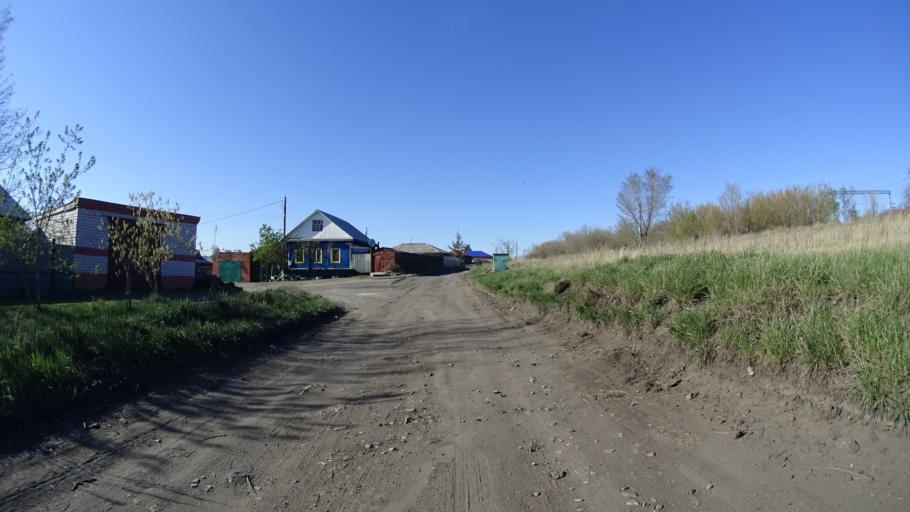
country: RU
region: Chelyabinsk
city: Troitsk
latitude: 54.0873
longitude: 61.5991
